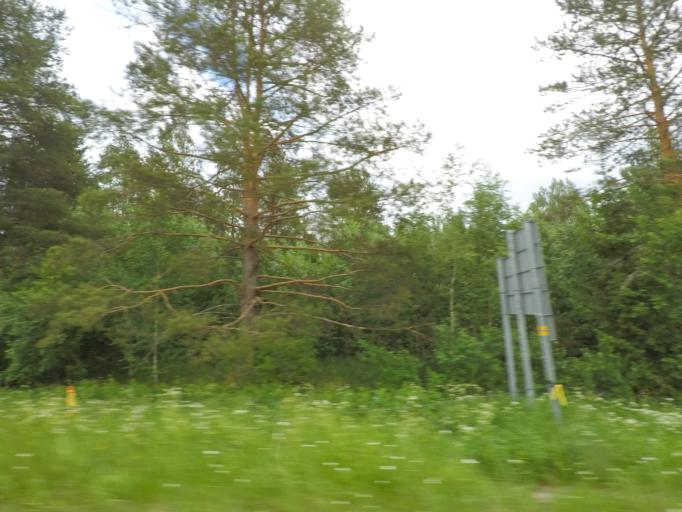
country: FI
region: Uusimaa
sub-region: Porvoo
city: Pukkila
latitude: 60.8022
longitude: 25.4752
